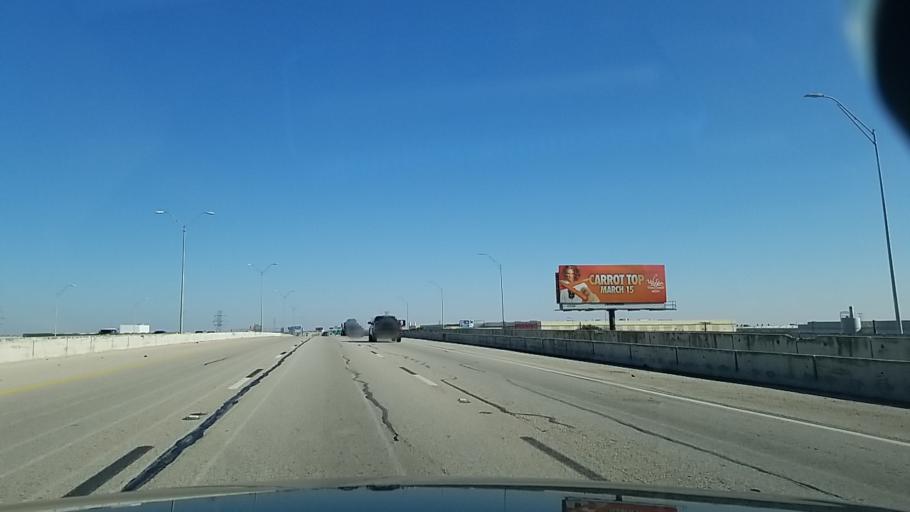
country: US
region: Texas
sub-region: Tarrant County
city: Saginaw
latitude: 32.8379
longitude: -97.3592
